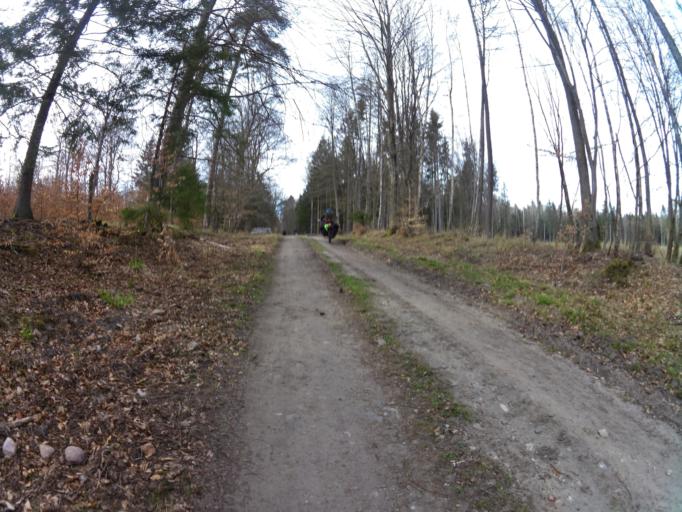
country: PL
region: West Pomeranian Voivodeship
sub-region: Powiat szczecinecki
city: Bialy Bor
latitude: 53.8902
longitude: 16.7185
